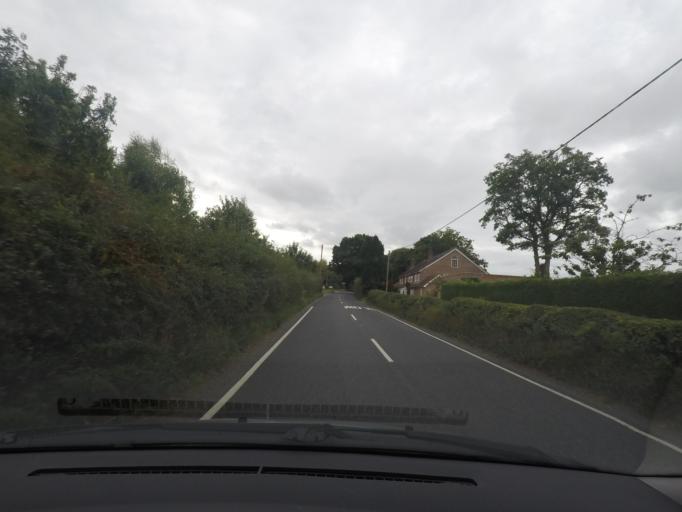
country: GB
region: England
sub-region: Wiltshire
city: Huish
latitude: 51.3860
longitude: -1.7572
